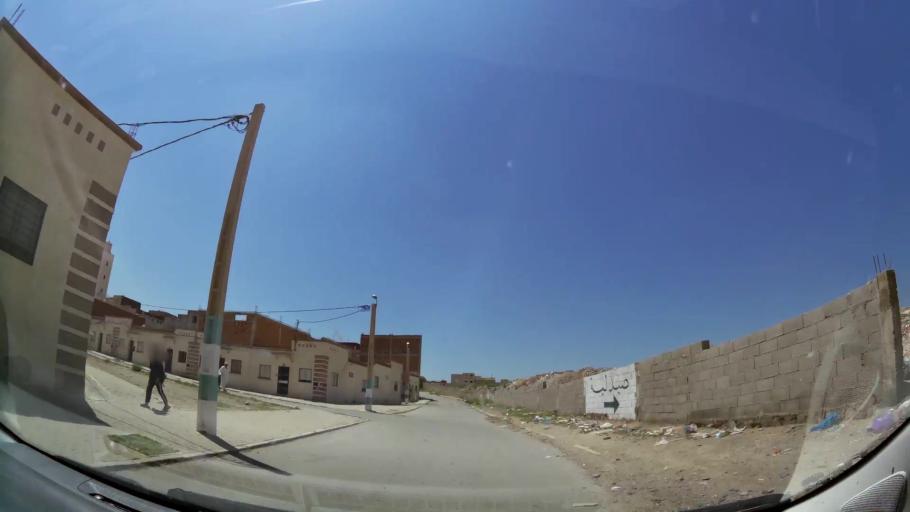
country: MA
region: Oriental
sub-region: Oujda-Angad
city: Oujda
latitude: 34.6912
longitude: -1.9496
